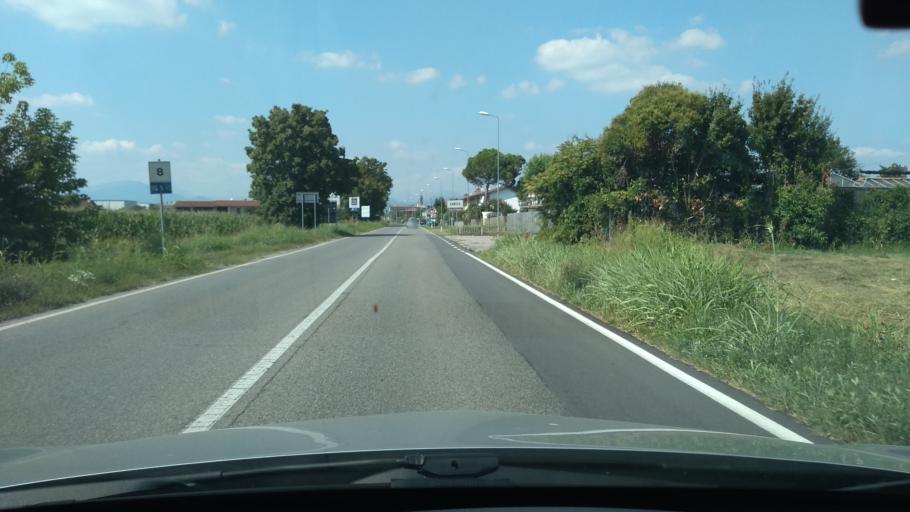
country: IT
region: Lombardy
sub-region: Provincia di Bergamo
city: Zanica
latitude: 45.6306
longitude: 9.6873
